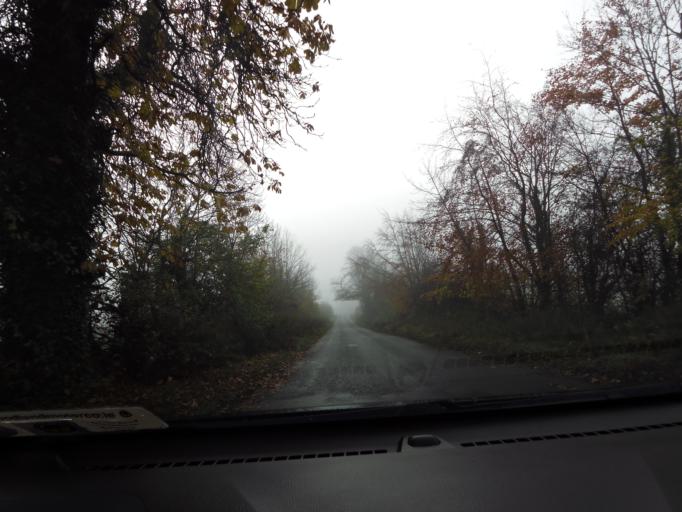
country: IE
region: Leinster
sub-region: An Iarmhi
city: Moate
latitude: 53.3830
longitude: -7.8033
